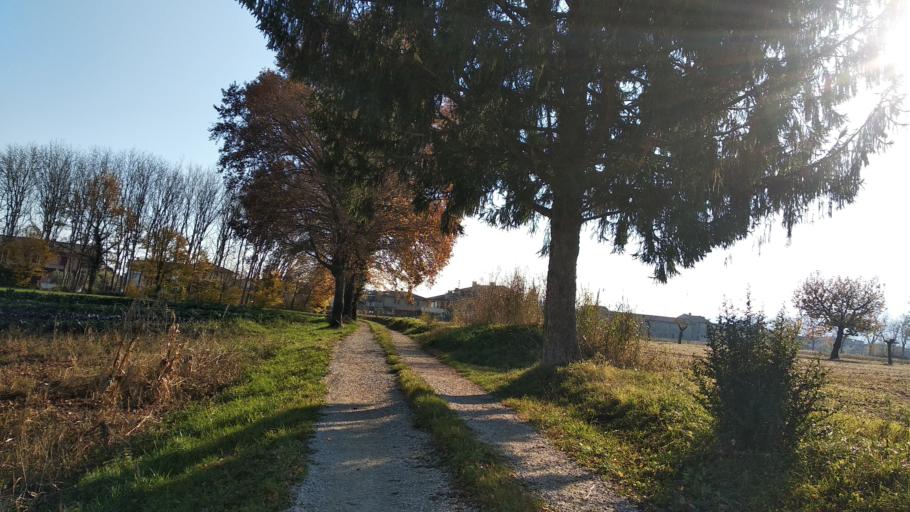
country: IT
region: Veneto
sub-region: Provincia di Vicenza
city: Schio
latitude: 45.7013
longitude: 11.3734
